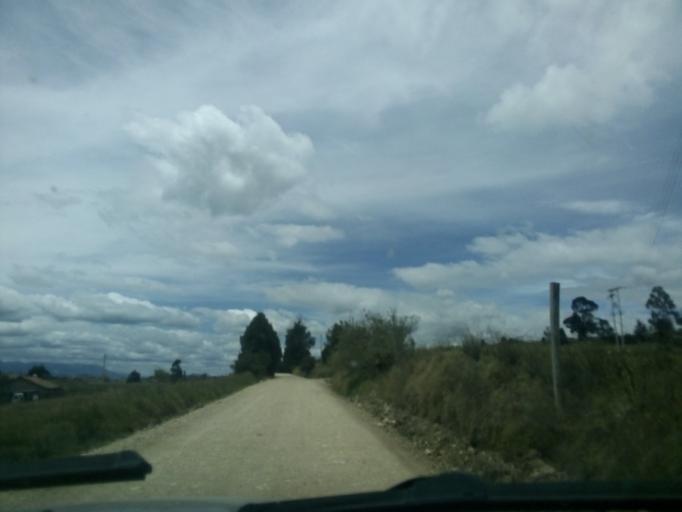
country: CO
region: Boyaca
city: Toca
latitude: 5.6000
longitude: -73.1559
